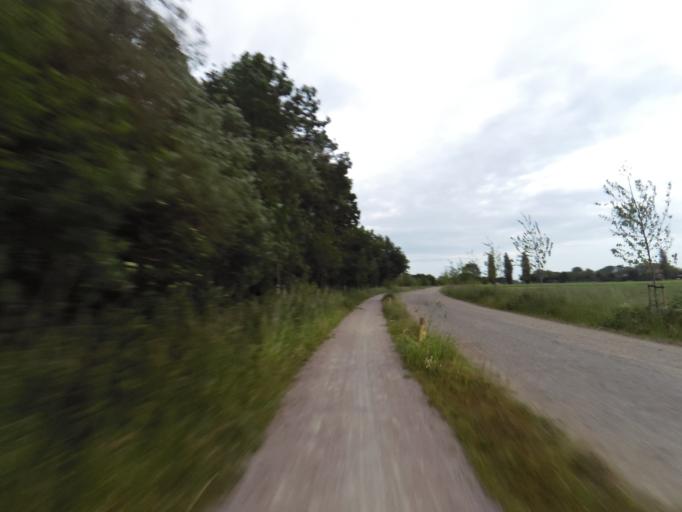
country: DE
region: North Rhine-Westphalia
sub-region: Regierungsbezirk Dusseldorf
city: Kleve
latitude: 51.8740
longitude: 6.1405
